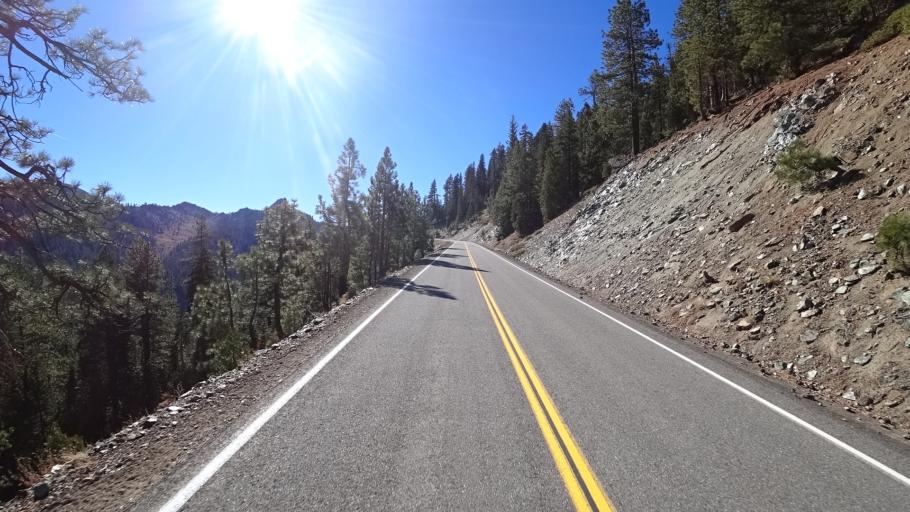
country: US
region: California
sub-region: Trinity County
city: Weaverville
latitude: 41.2256
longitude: -122.8961
